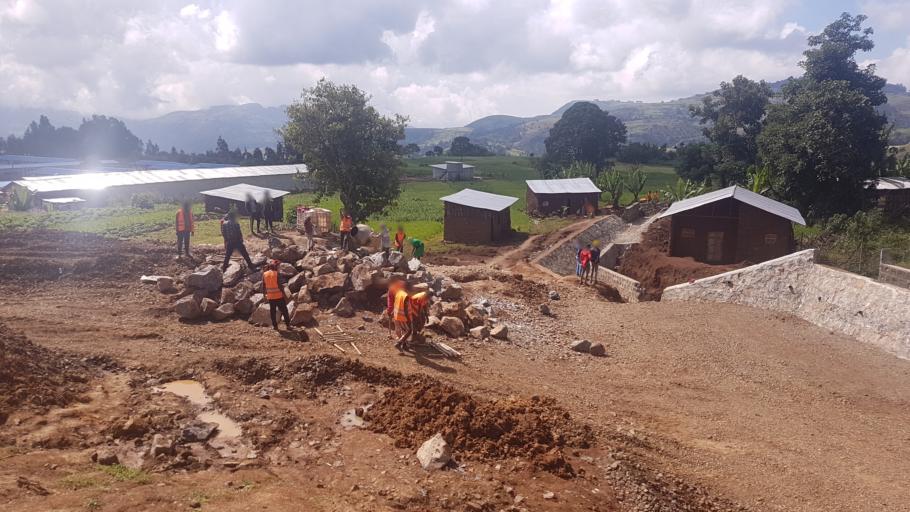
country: ET
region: Southern Nations, Nationalities, and People's Region
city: Arba Minch'
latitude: 6.3227
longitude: 37.5370
